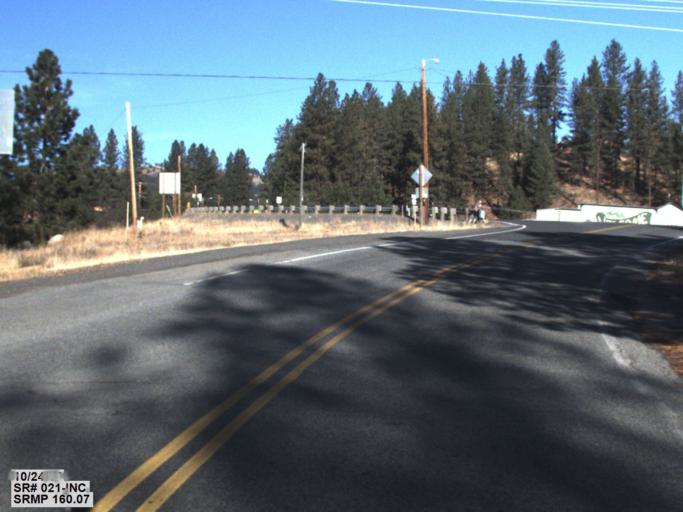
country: US
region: Washington
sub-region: Ferry County
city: Republic
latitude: 48.6399
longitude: -118.7339
